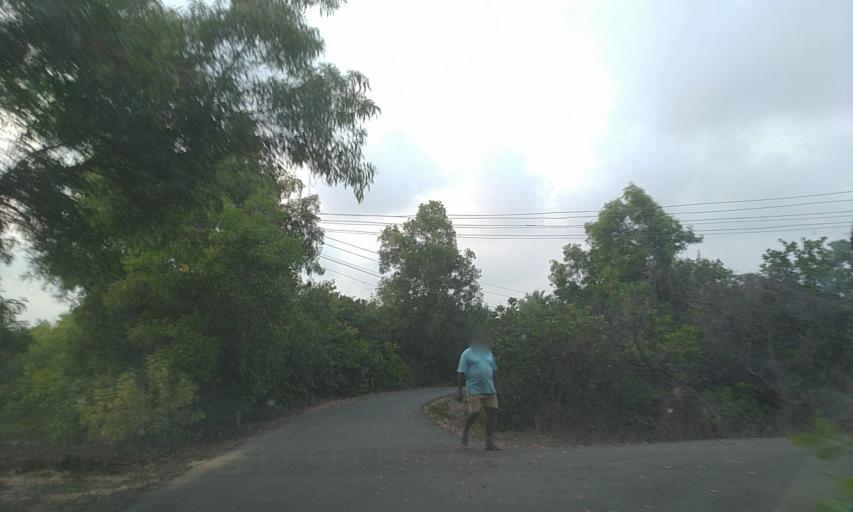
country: IN
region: Goa
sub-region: South Goa
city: Cavelossim
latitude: 15.1821
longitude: 73.9445
